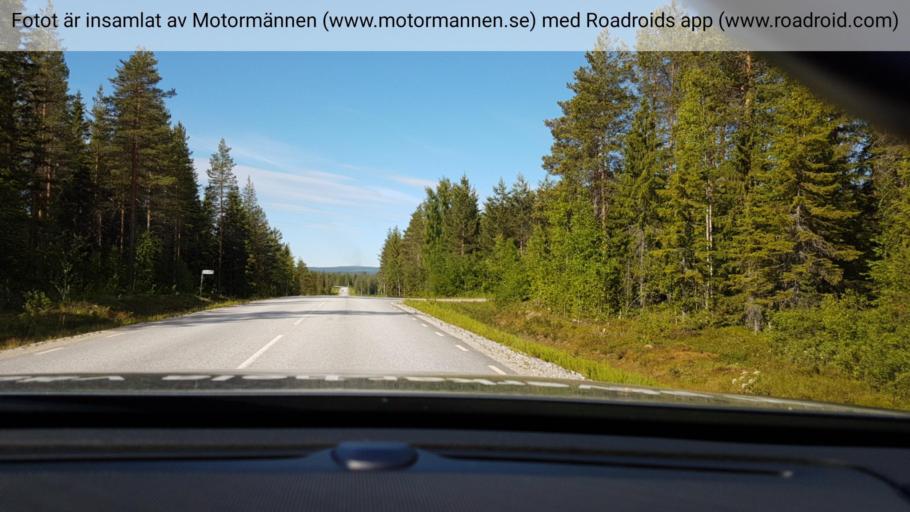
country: SE
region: Vaesterbotten
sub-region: Bjurholms Kommun
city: Bjurholm
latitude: 64.1662
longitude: 19.3838
